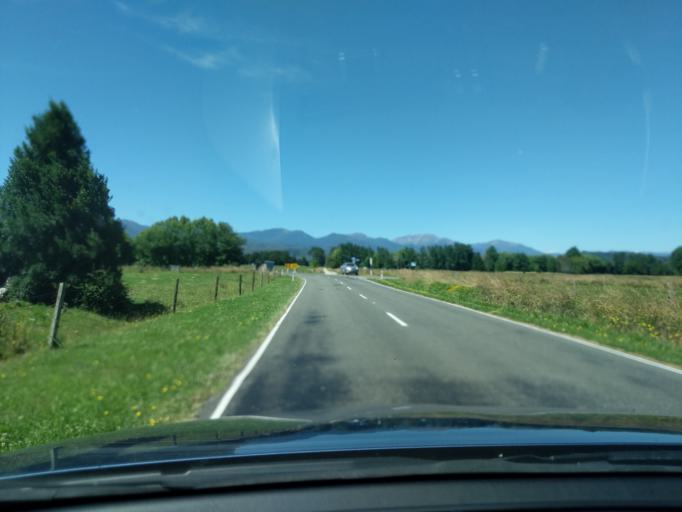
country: NZ
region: Tasman
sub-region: Tasman District
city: Takaka
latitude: -40.7005
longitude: 172.6322
